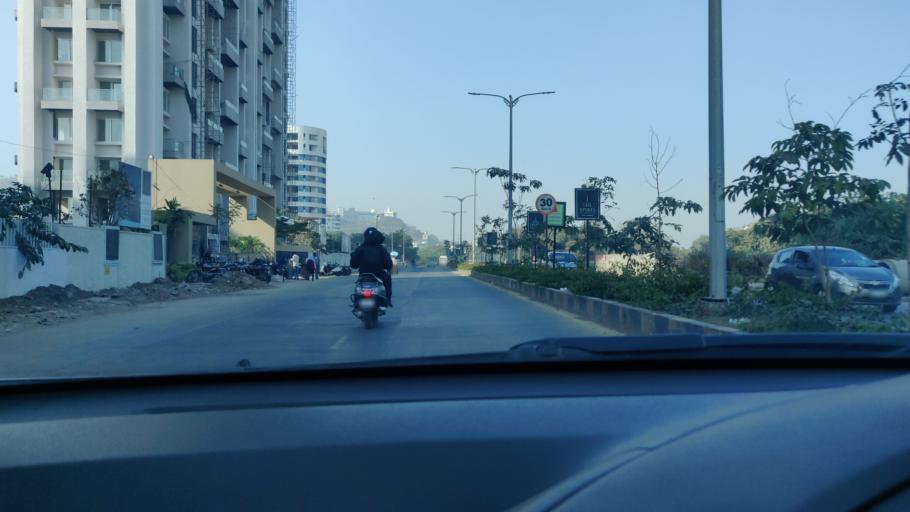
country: IN
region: Maharashtra
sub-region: Pune Division
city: Khadki
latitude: 18.5633
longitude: 73.7962
